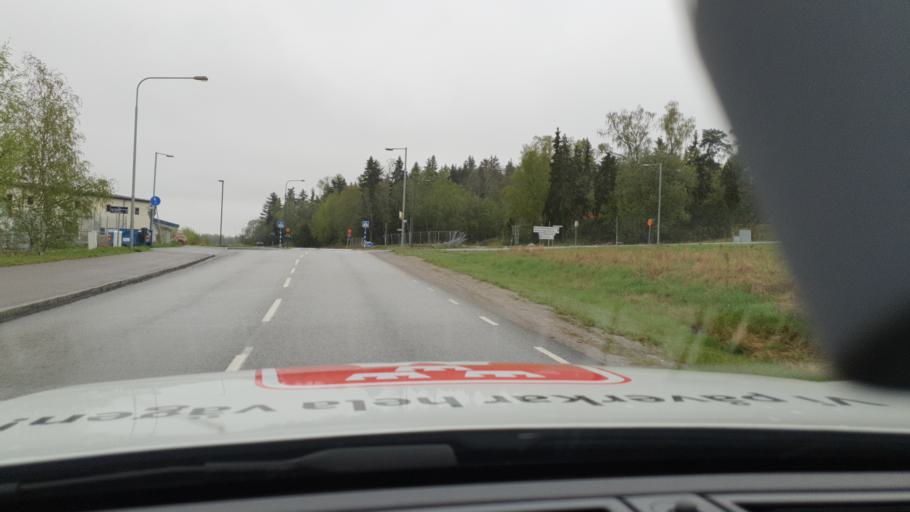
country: SE
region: Stockholm
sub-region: Osterakers Kommun
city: Akersberga
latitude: 59.4800
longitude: 18.2751
